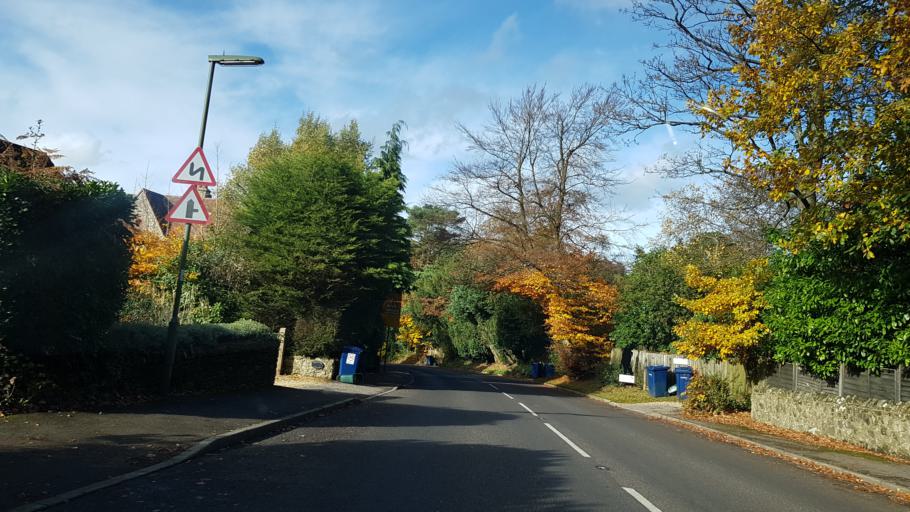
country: GB
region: England
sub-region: Surrey
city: Hindhead
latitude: 51.1243
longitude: -0.7444
